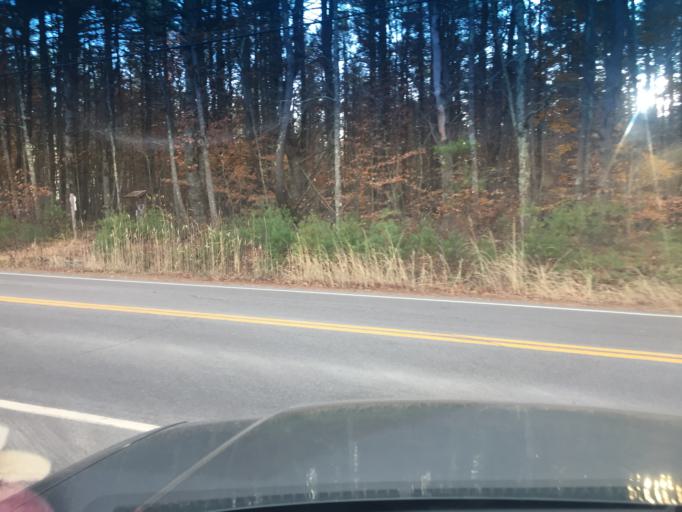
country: US
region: Maine
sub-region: York County
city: York Harbor
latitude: 43.1719
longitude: -70.7173
